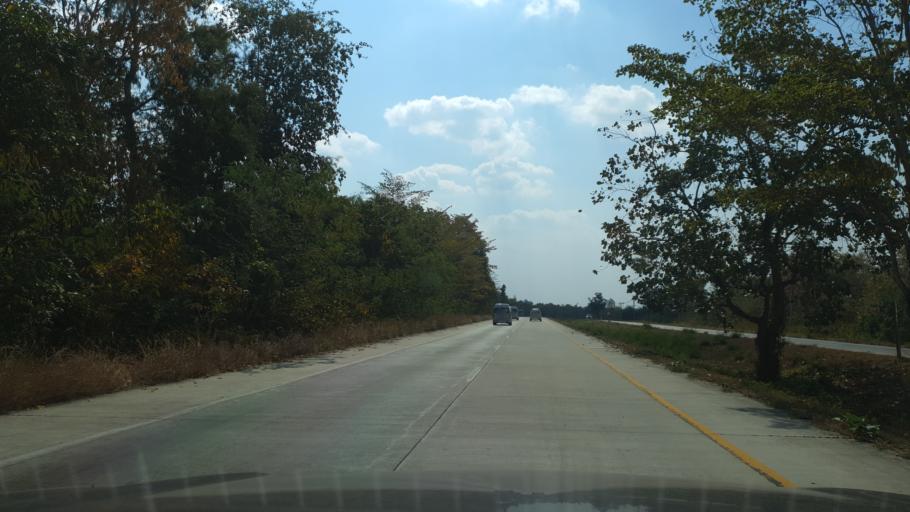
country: TH
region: Lampang
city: Mae Phrik
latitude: 17.3091
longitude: 99.1488
